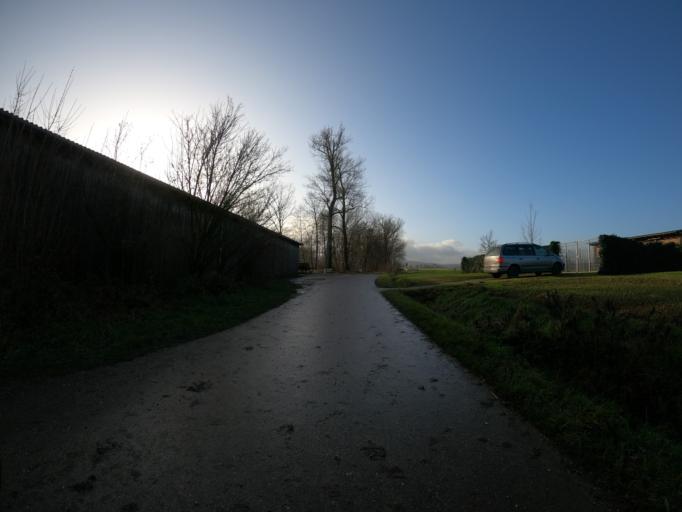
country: DE
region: Baden-Wuerttemberg
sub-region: Regierungsbezirk Stuttgart
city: Boll
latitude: 48.6667
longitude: 9.6243
